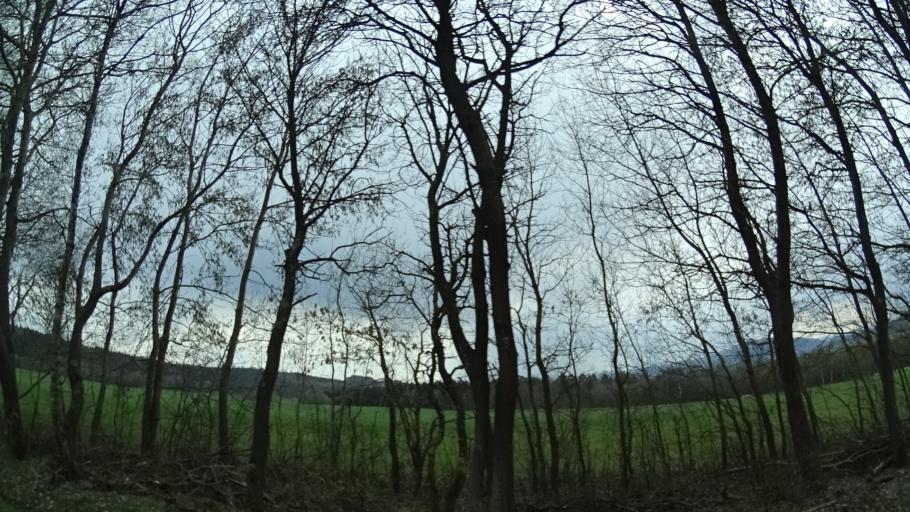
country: DE
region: Rheinland-Pfalz
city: Henau
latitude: 49.8769
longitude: 7.5259
